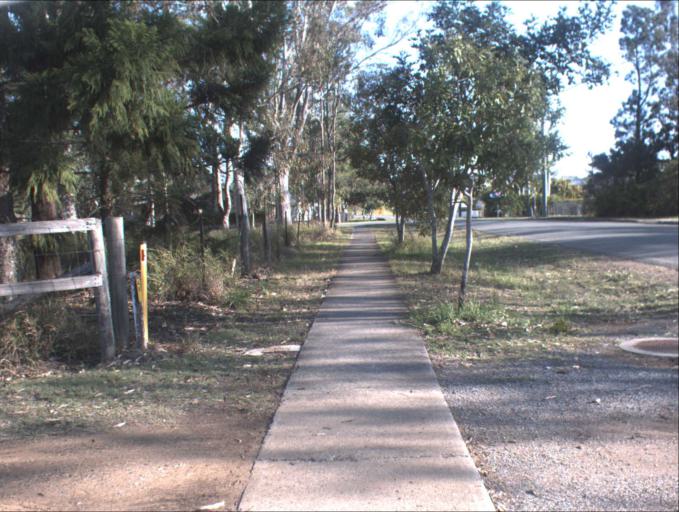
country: AU
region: Queensland
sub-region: Logan
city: Chambers Flat
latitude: -27.7666
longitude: 153.1050
